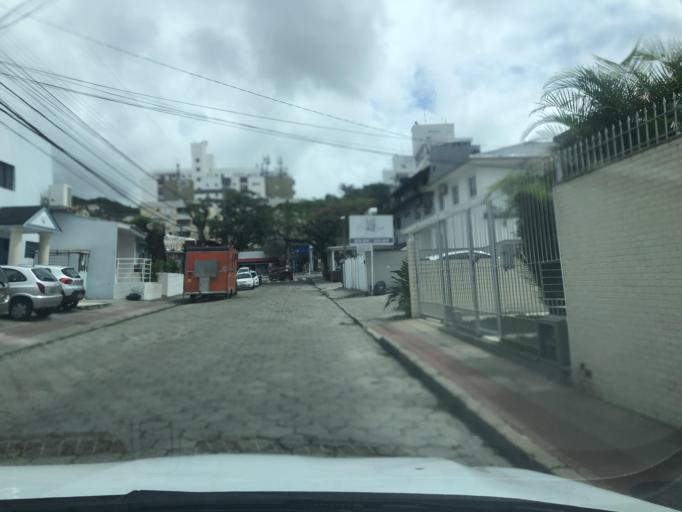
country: BR
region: Santa Catarina
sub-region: Florianopolis
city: Corrego Grande
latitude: -27.6000
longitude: -48.5134
